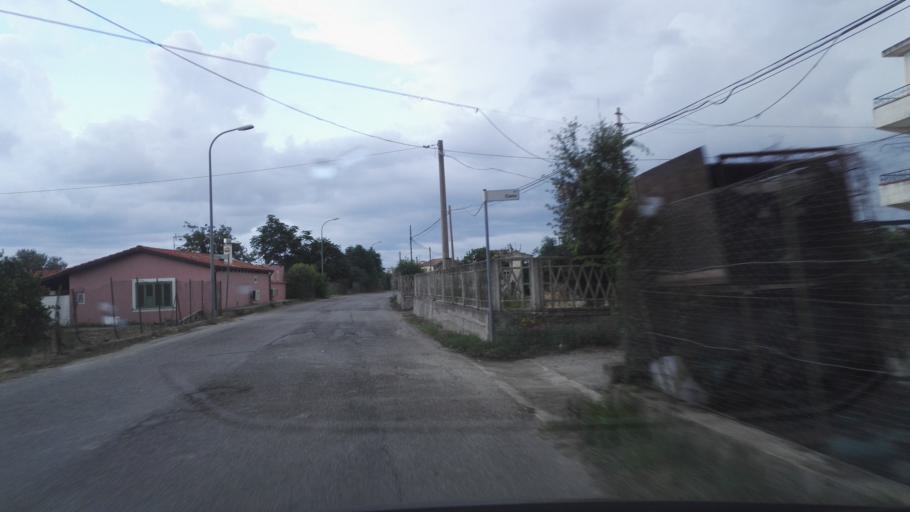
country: IT
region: Calabria
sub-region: Provincia di Reggio Calabria
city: Caulonia Marina
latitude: 38.3567
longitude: 16.4699
